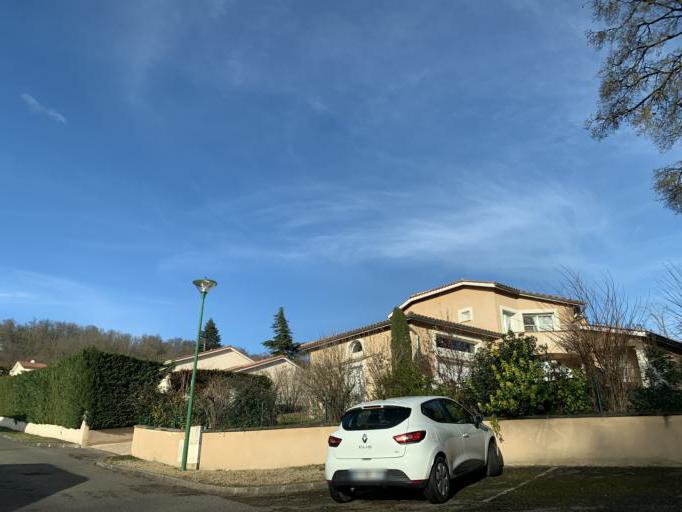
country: FR
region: Rhone-Alpes
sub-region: Departement de l'Ain
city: La Boisse
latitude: 45.8478
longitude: 5.0405
